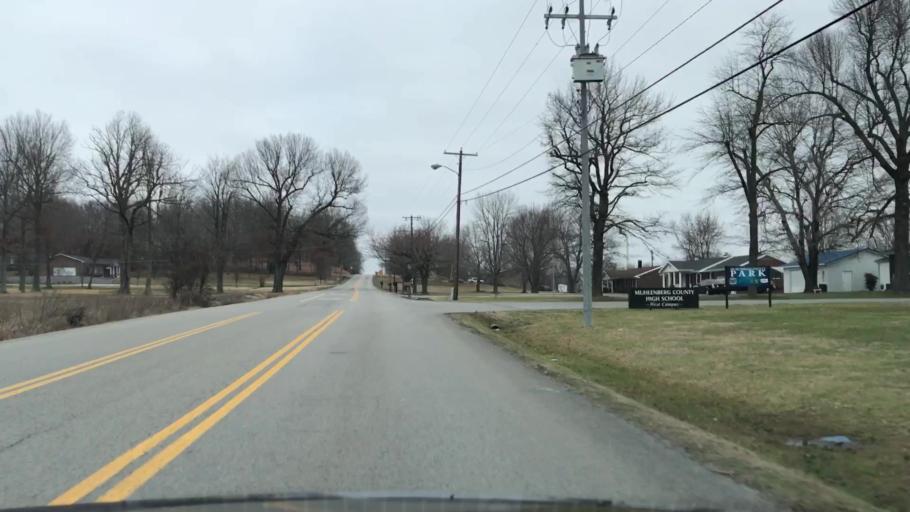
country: US
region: Kentucky
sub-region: Muhlenberg County
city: Greenville
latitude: 37.2236
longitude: -87.1937
